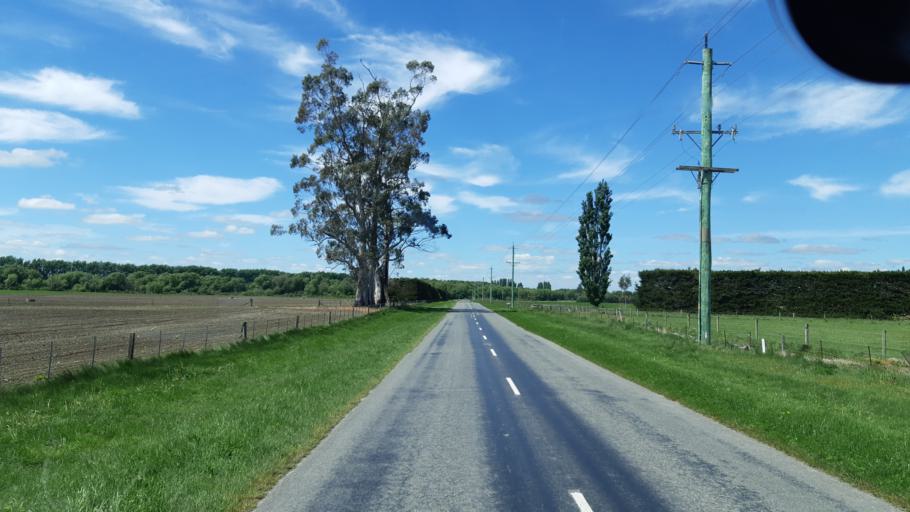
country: NZ
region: Canterbury
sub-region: Ashburton District
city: Methven
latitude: -43.7314
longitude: 171.5203
